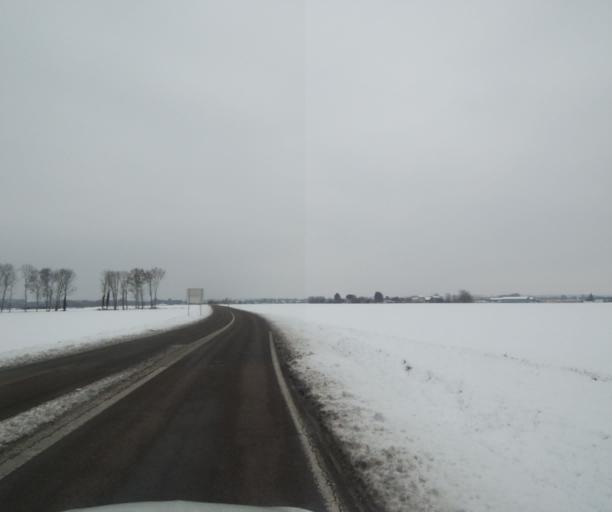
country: FR
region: Champagne-Ardenne
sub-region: Departement de la Haute-Marne
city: Saint-Dizier
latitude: 48.6207
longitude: 4.9279
